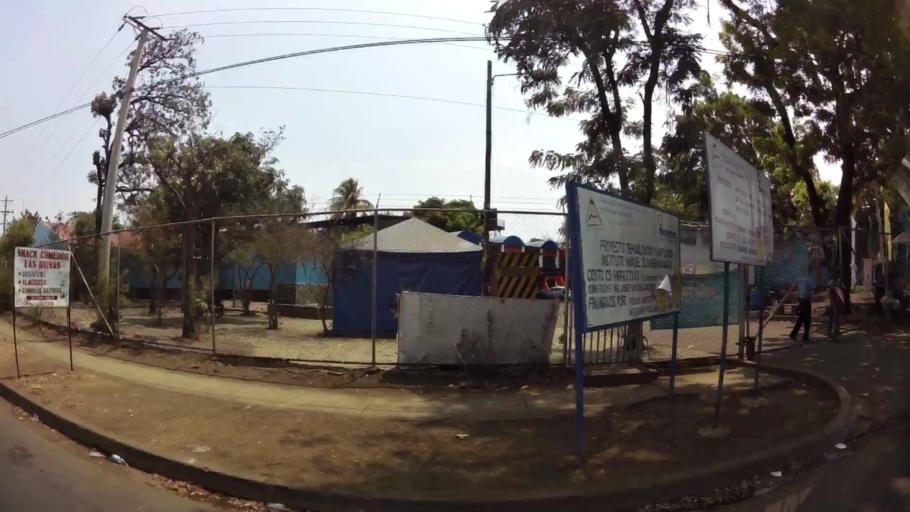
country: NI
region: Managua
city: Ciudad Sandino
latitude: 12.1525
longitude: -86.3097
